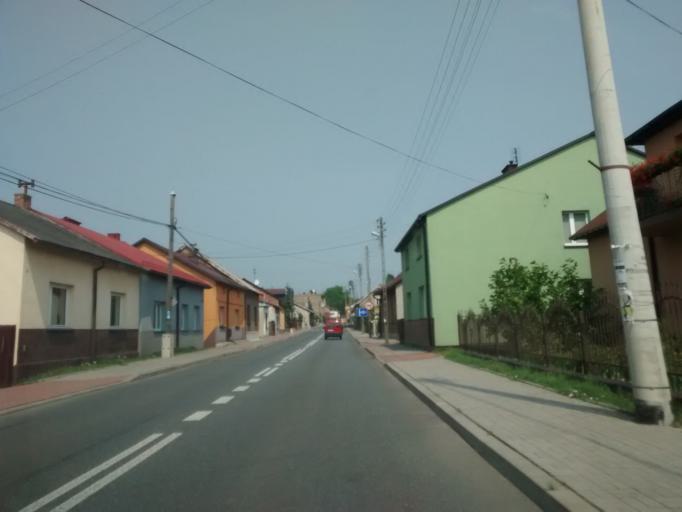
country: PL
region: Silesian Voivodeship
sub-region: Powiat zawiercianski
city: Ogrodzieniec
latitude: 50.4492
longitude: 19.5235
